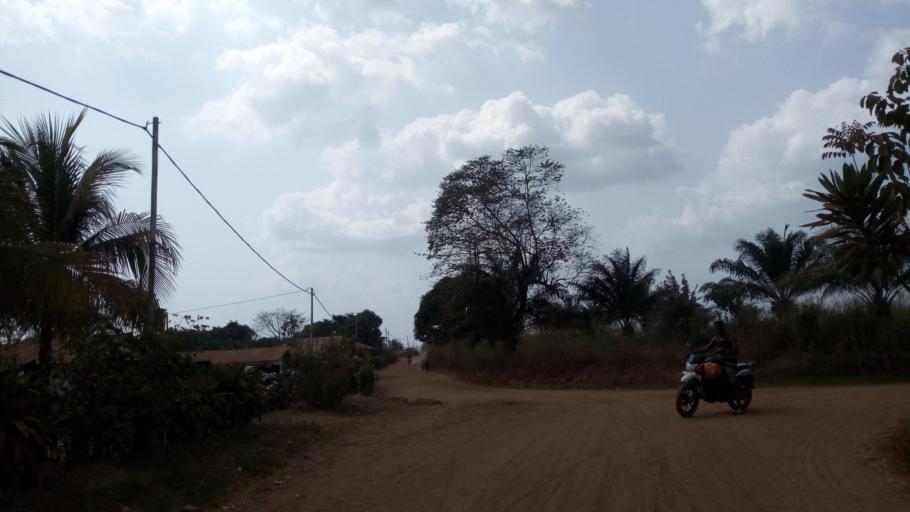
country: SL
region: Southern Province
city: Mogbwemo
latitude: 7.7758
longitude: -12.2983
